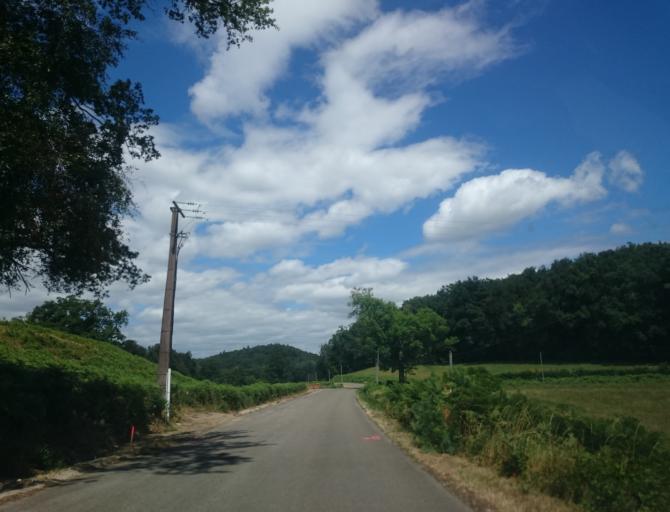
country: FR
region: Auvergne
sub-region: Departement du Cantal
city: Laroquebrou
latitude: 44.9124
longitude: 2.1911
